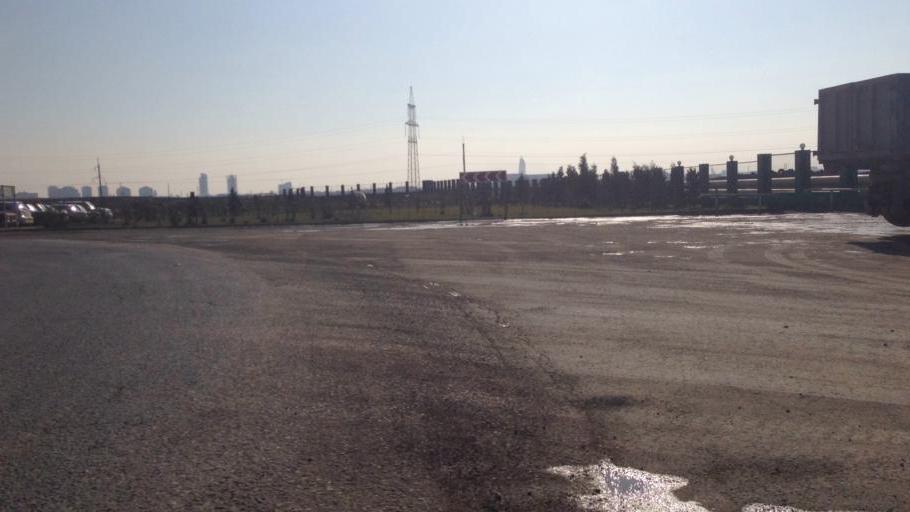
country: AZ
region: Baki
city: Balakhani
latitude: 40.4538
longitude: 49.8933
